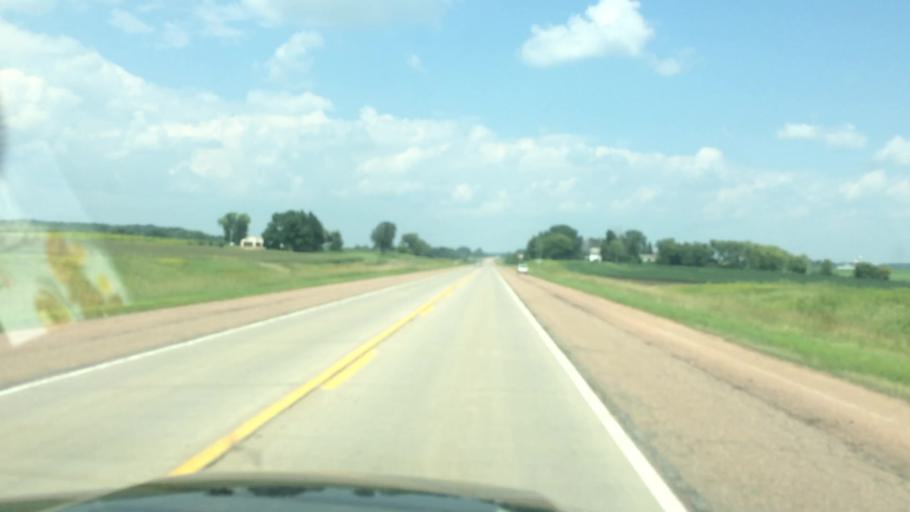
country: US
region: Wisconsin
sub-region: Clark County
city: Colby
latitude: 44.8658
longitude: -90.3158
